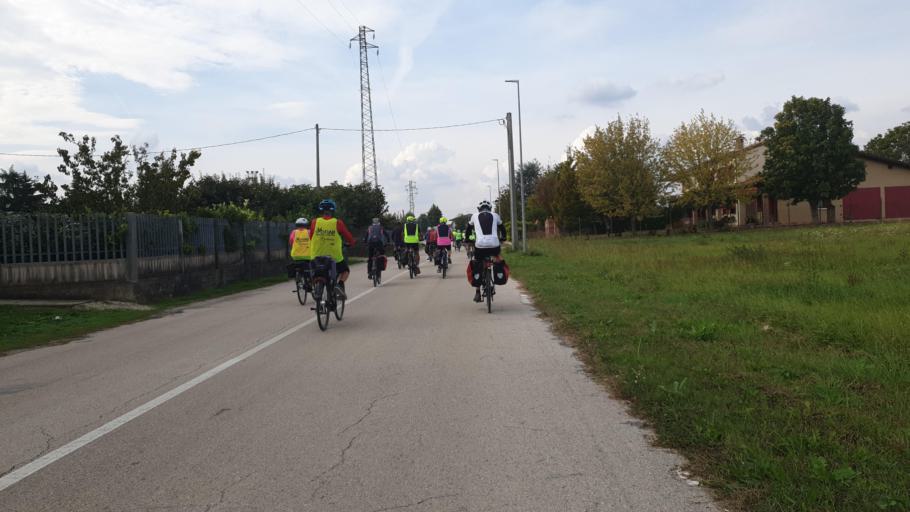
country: IT
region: Veneto
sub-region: Provincia di Vicenza
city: Poiana Maggiore
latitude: 45.2900
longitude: 11.5079
